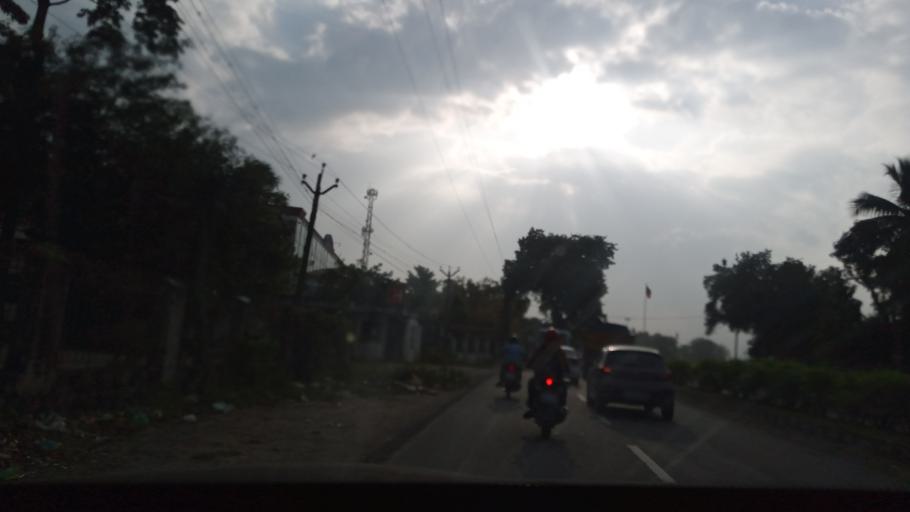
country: IN
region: Tamil Nadu
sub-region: Kancheepuram
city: Vengavasal
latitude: 12.8616
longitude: 80.1300
